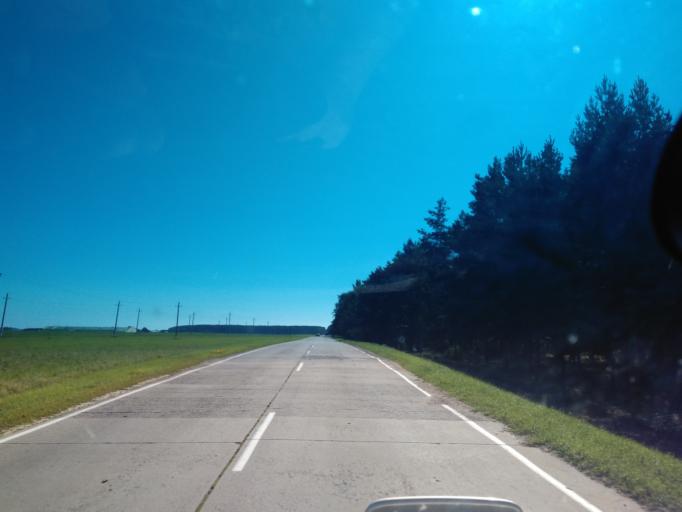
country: BY
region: Minsk
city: Stan'kava
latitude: 53.6258
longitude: 27.2674
